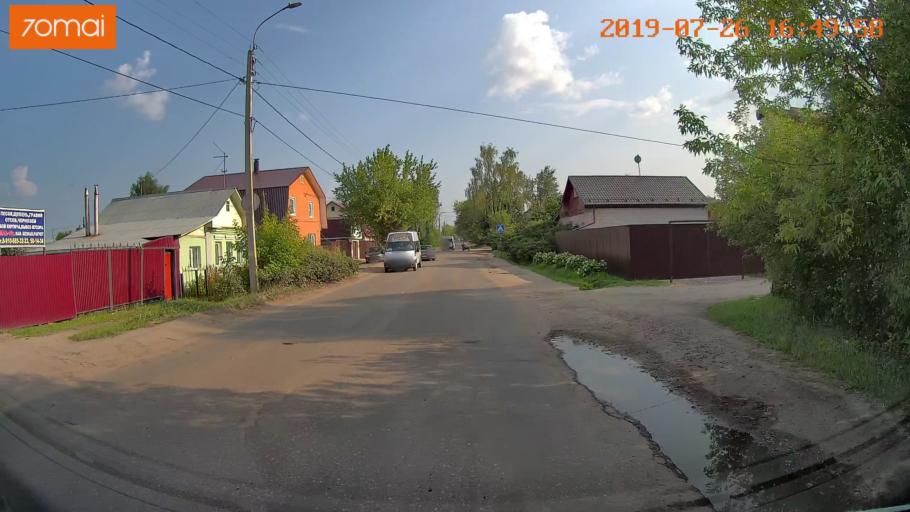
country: RU
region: Ivanovo
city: Bogorodskoye
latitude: 57.0263
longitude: 41.0207
